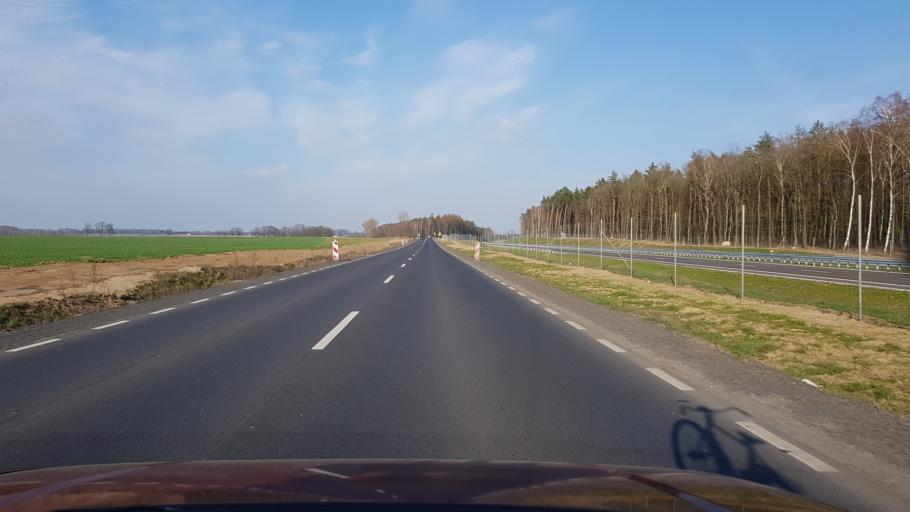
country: PL
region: West Pomeranian Voivodeship
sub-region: Powiat gryficki
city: Ploty
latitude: 53.8406
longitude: 15.3069
